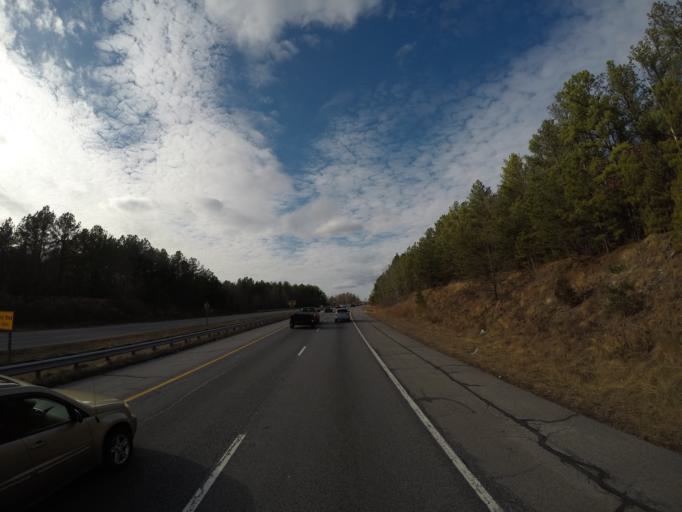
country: US
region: Maryland
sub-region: Prince George's County
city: Accokeek
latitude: 38.6579
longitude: -77.0093
